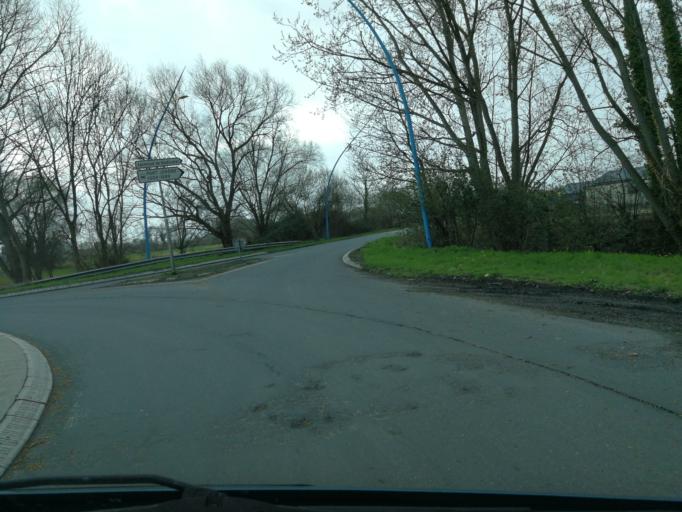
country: FR
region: Haute-Normandie
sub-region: Departement de l'Eure
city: Quillebeuf-sur-Seine
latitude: 49.4840
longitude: 0.5313
